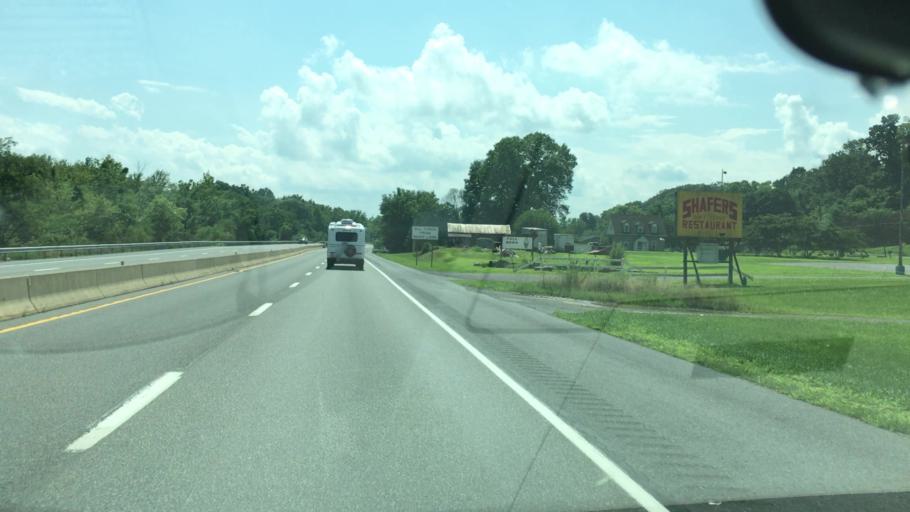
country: US
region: Pennsylvania
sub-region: Snyder County
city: Selinsgrove
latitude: 40.6889
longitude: -76.8834
